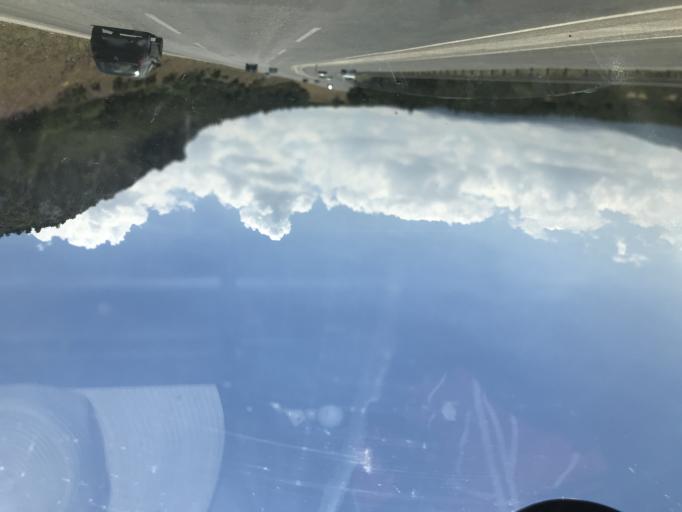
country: TR
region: Denizli
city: Honaz
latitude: 37.7127
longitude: 29.2056
